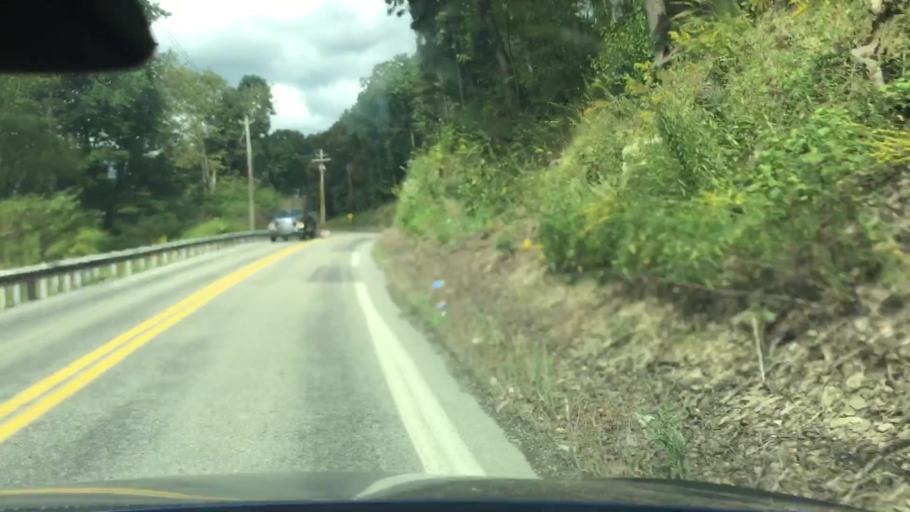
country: US
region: Pennsylvania
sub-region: Allegheny County
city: Curtisville
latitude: 40.6470
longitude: -79.8388
